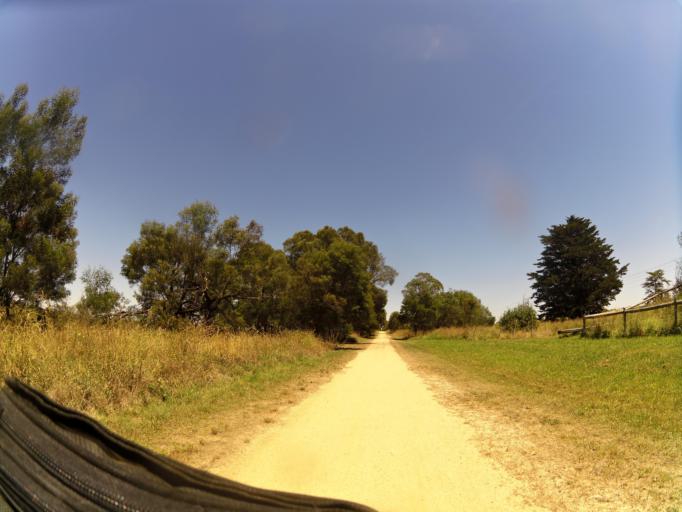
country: AU
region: Victoria
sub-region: Wellington
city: Sale
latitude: -37.9778
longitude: 147.0332
